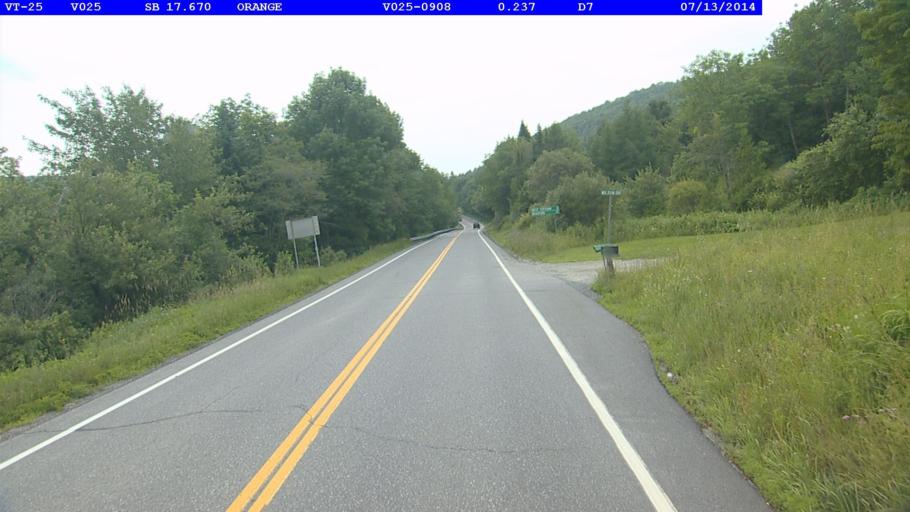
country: US
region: Vermont
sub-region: Washington County
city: South Barre
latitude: 44.1395
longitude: -72.3204
